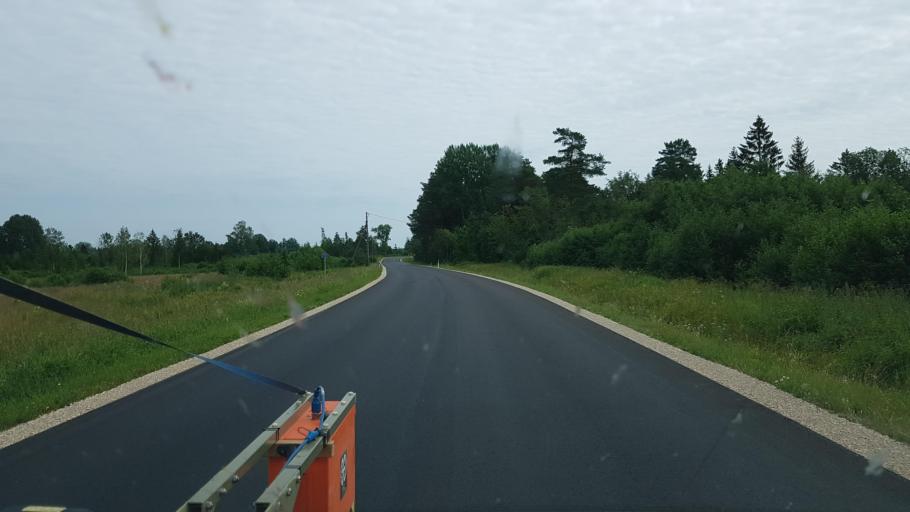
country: EE
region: Paernumaa
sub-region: Halinga vald
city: Parnu-Jaagupi
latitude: 58.6193
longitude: 24.2941
